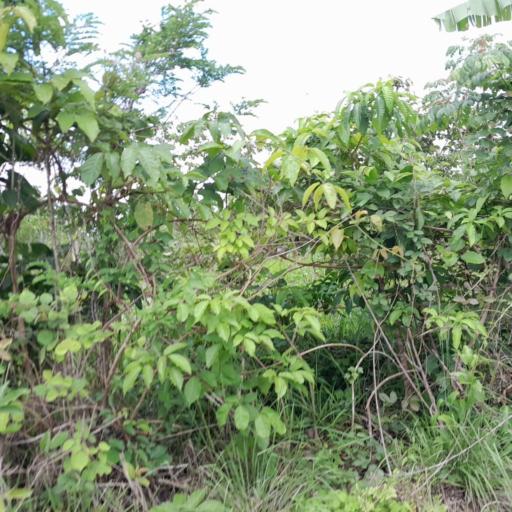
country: PE
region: Ucayali
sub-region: Provincia de Coronel Portillo
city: Puerto Callao
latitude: -8.2706
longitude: -74.6468
